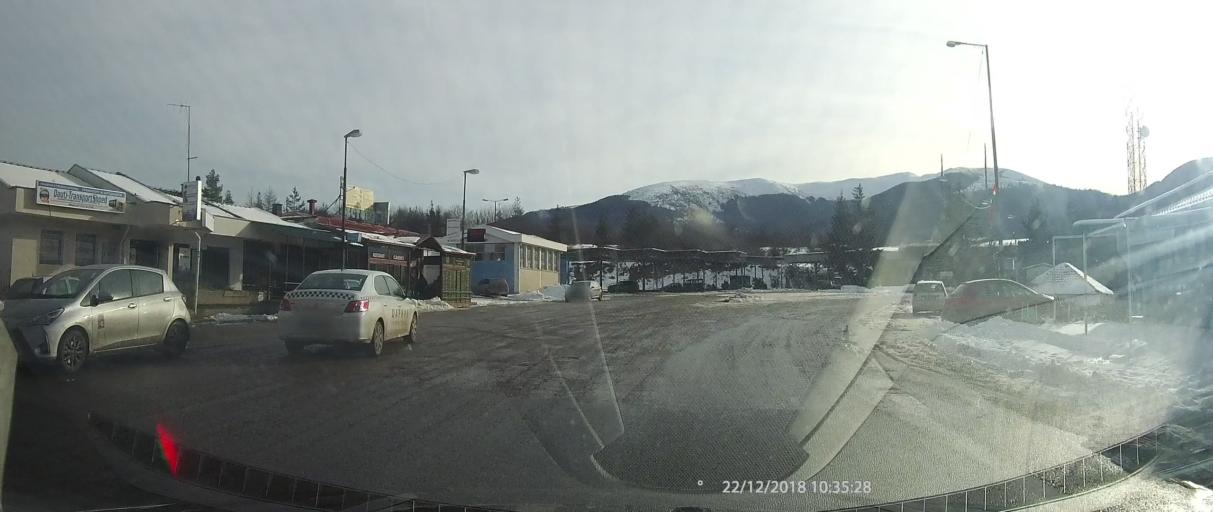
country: MK
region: Kriva Palanka
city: Kriva Palanka
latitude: 42.2215
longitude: 22.4571
